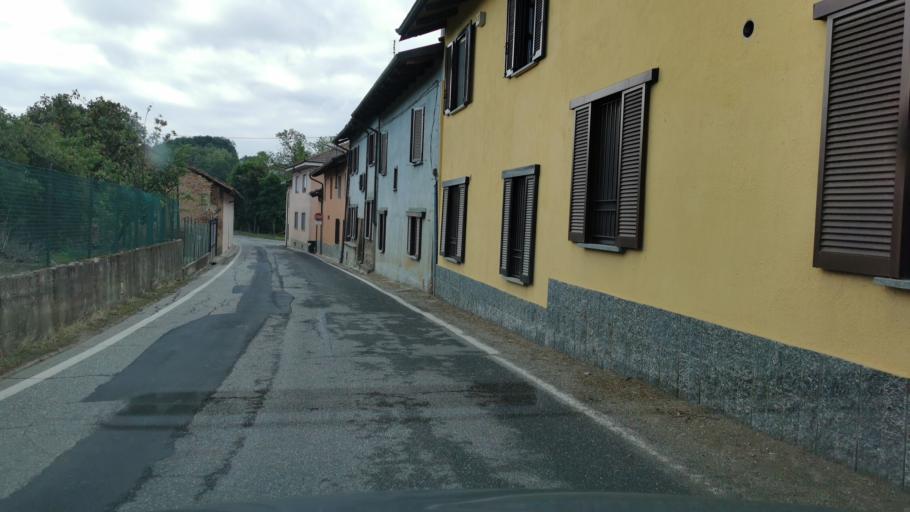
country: IT
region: Piedmont
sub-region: Provincia di Torino
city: Cambiano
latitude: 44.9985
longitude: 7.7834
